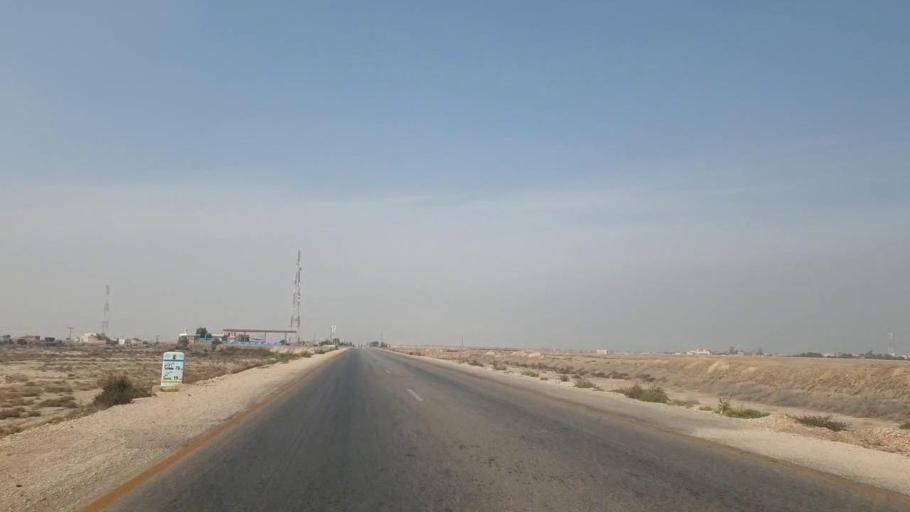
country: PK
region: Sindh
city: Sann
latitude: 25.8983
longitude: 68.2344
